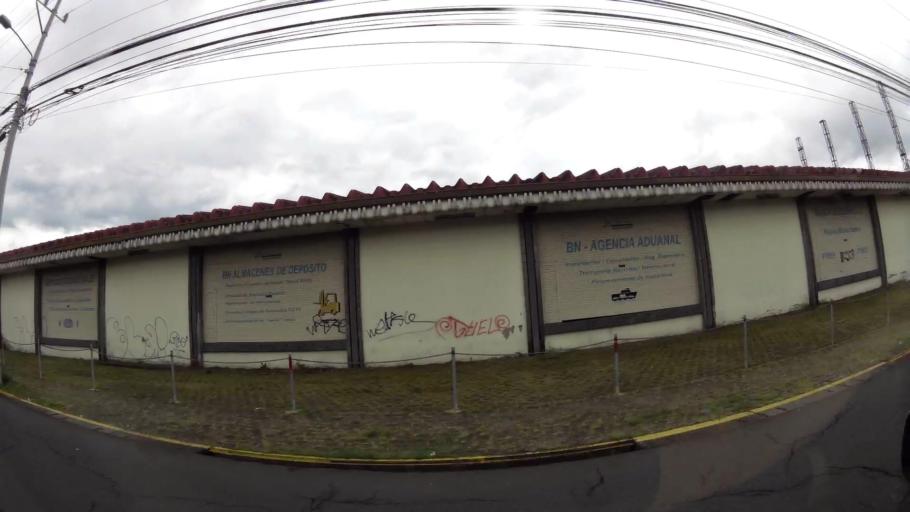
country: CR
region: San Jose
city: Calle Blancos
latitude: 9.9450
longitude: -84.0682
